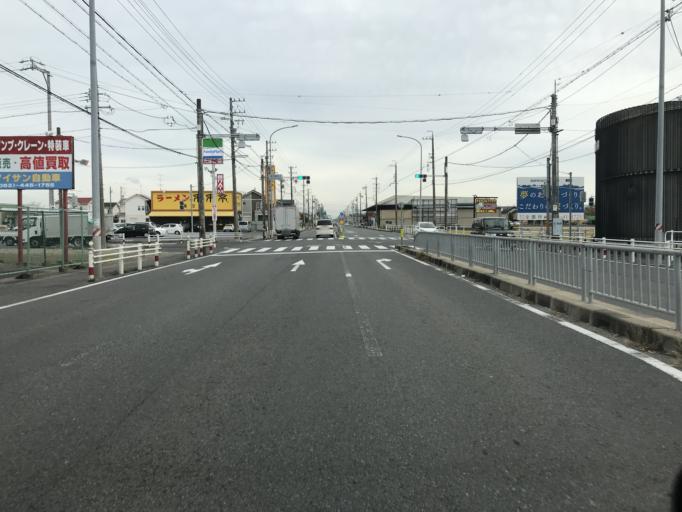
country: JP
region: Aichi
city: Kanie
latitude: 35.1848
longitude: 136.7927
